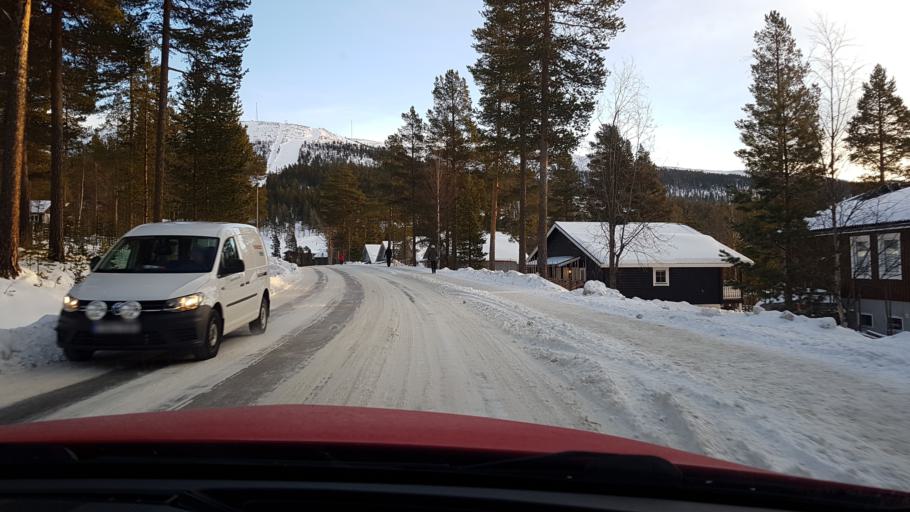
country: SE
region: Jaemtland
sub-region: Harjedalens Kommun
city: Sveg
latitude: 62.4213
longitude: 13.9496
